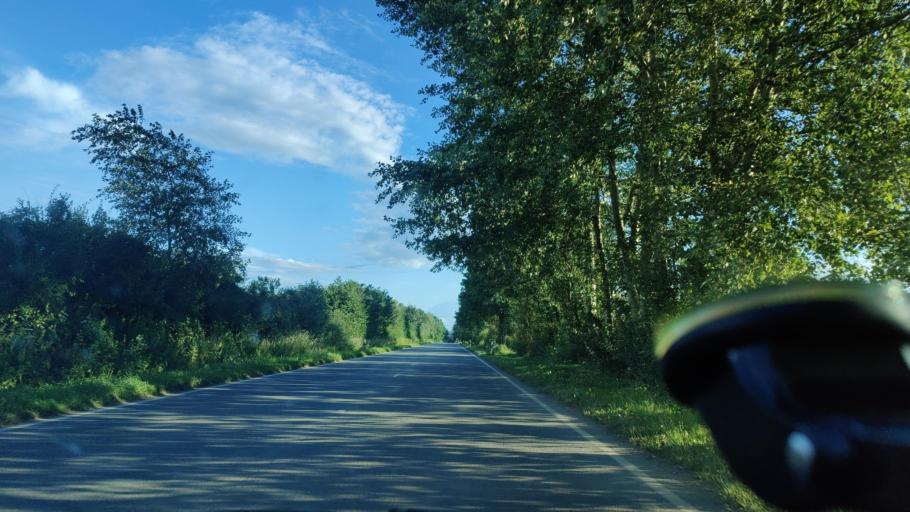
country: DE
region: North Rhine-Westphalia
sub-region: Regierungsbezirk Dusseldorf
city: Schermbeck
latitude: 51.6084
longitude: 6.8909
